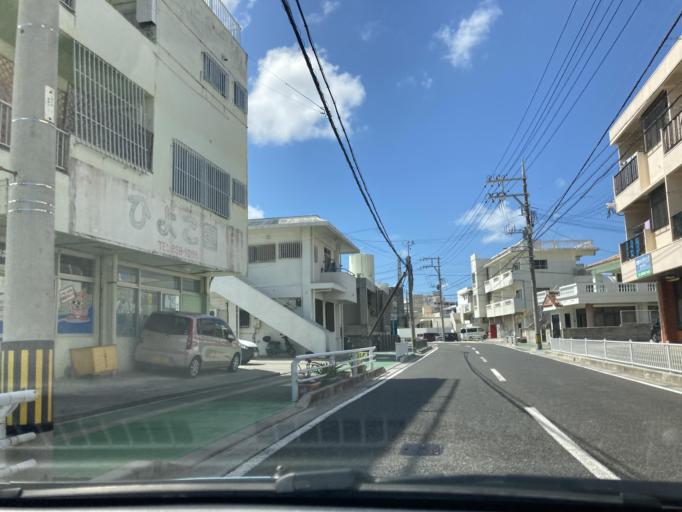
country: JP
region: Okinawa
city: Tomigusuku
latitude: 26.1964
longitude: 127.6718
